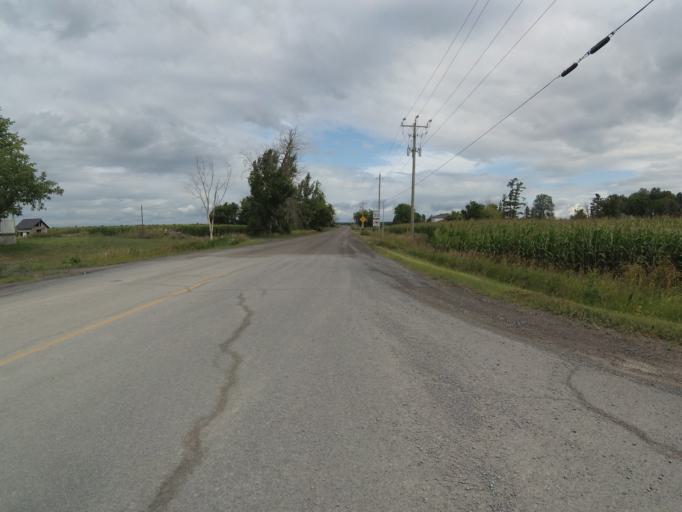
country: CA
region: Ontario
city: Clarence-Rockland
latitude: 45.4502
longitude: -75.2944
